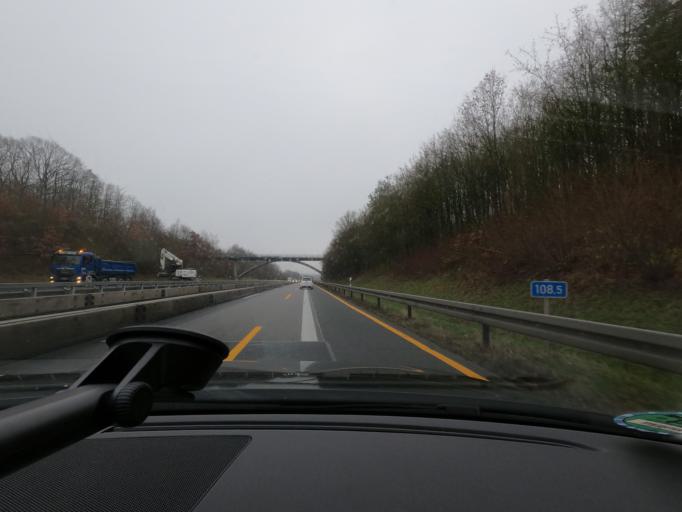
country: DE
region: Bavaria
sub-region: Upper Franconia
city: Strullendorf
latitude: 49.8482
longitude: 10.9921
